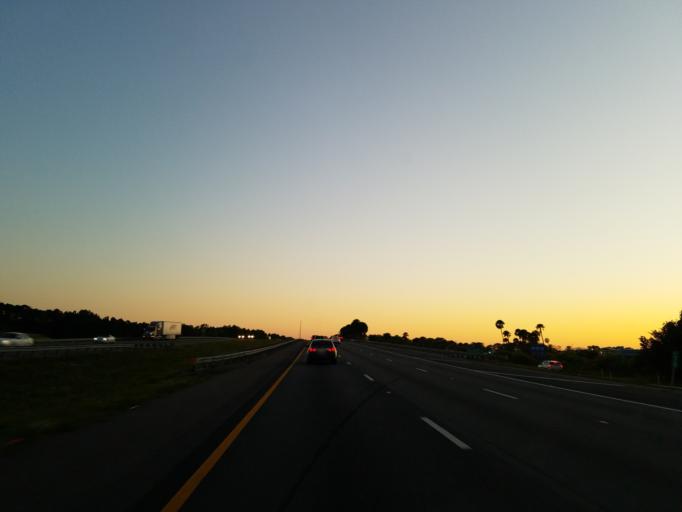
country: US
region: Florida
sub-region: Polk County
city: Loughman
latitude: 28.2632
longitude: -81.6110
